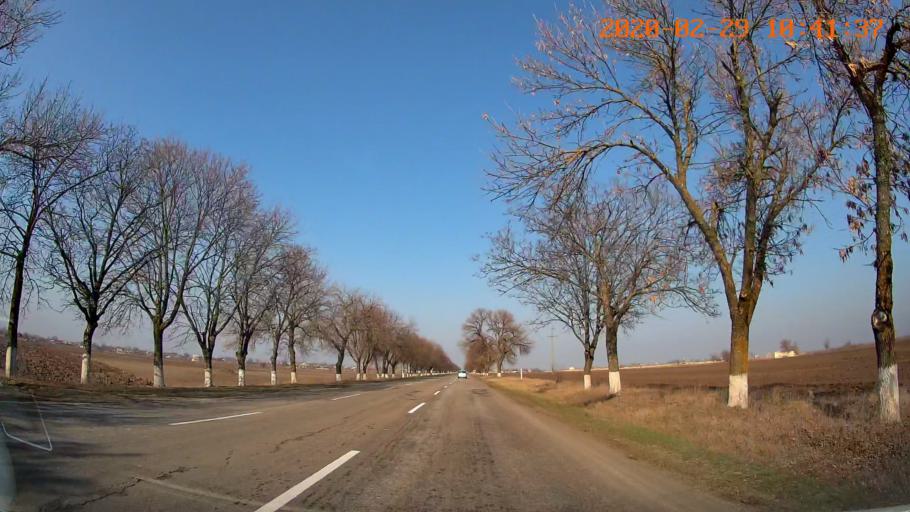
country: MD
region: Telenesti
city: Grigoriopol
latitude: 47.0441
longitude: 29.4226
